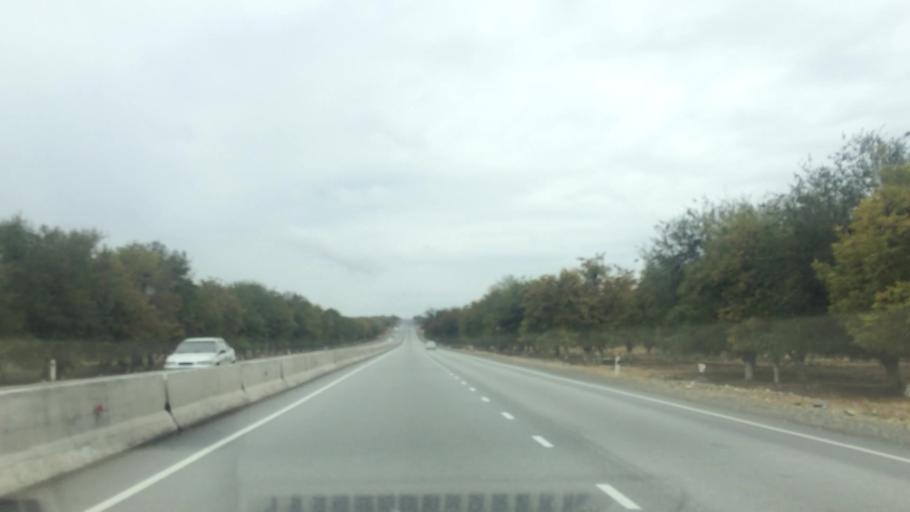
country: UZ
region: Samarqand
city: Bulung'ur
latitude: 39.8721
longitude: 67.4791
